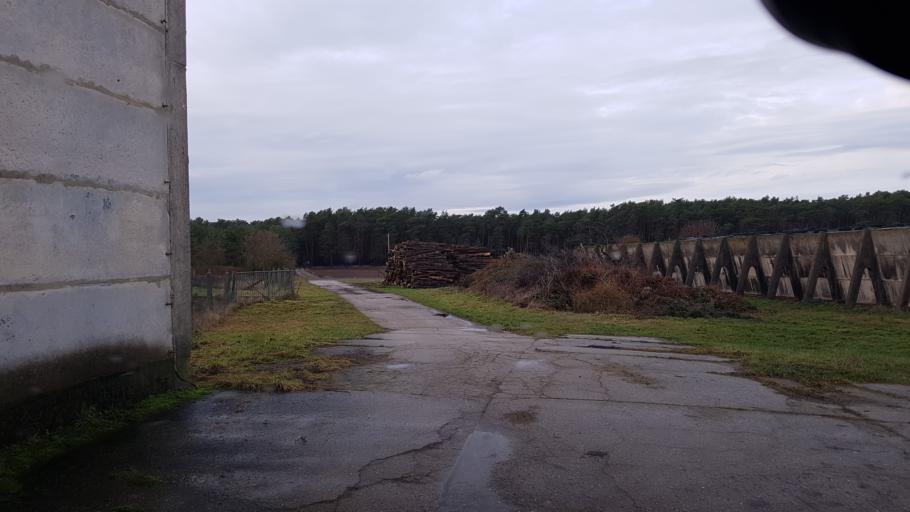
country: DE
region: Brandenburg
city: Hohenbucko
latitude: 51.7635
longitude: 13.4616
